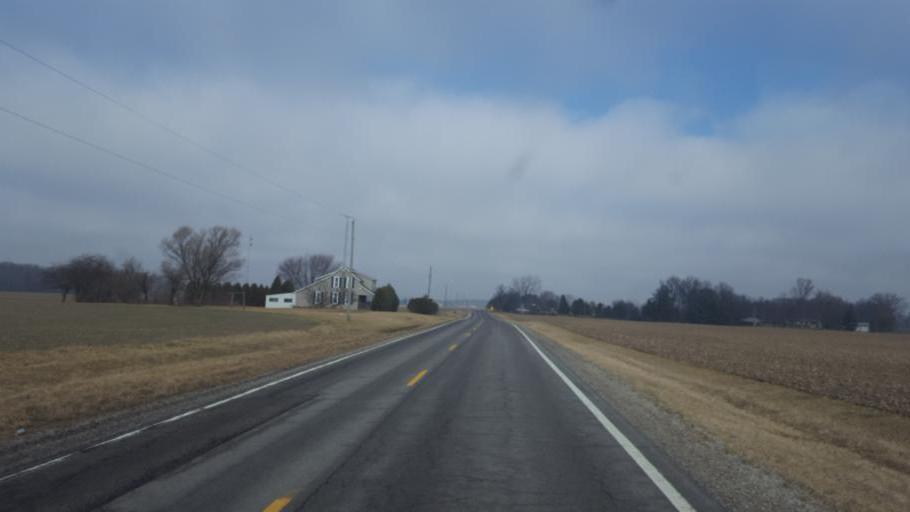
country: US
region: Ohio
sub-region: Crawford County
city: Galion
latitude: 40.7091
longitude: -82.8749
